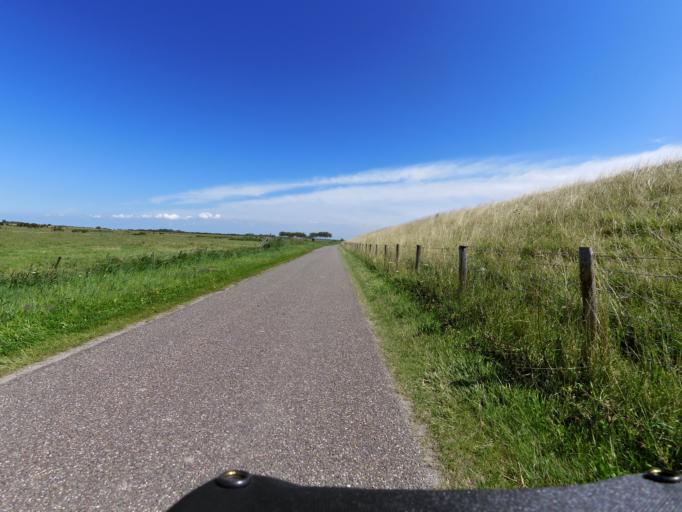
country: NL
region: South Holland
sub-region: Gemeente Goeree-Overflakkee
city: Goedereede
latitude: 51.8040
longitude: 3.9627
